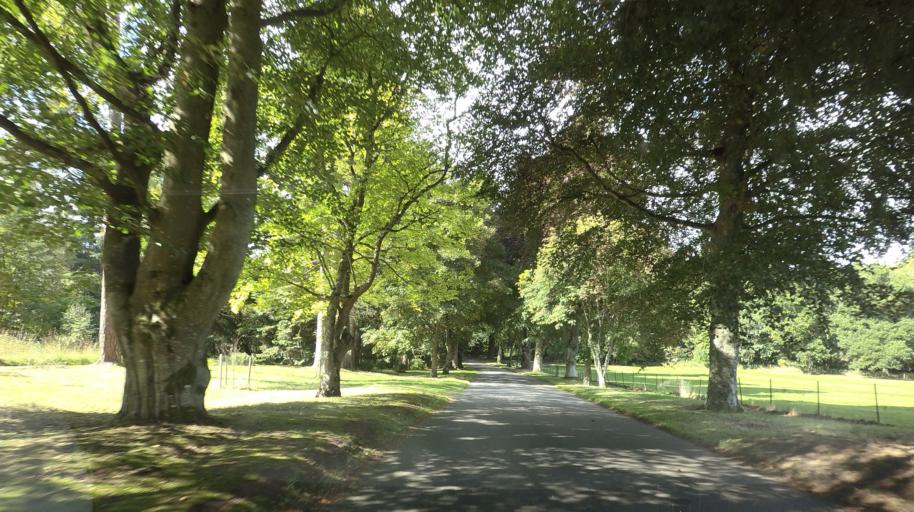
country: GB
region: Scotland
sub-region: Aberdeenshire
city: Banchory
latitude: 57.0598
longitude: -2.4338
